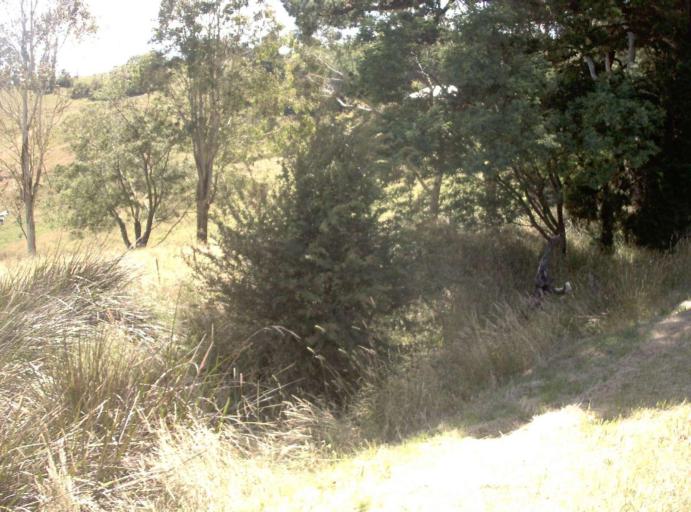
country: AU
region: Victoria
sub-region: Baw Baw
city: Warragul
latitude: -38.3597
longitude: 145.8726
